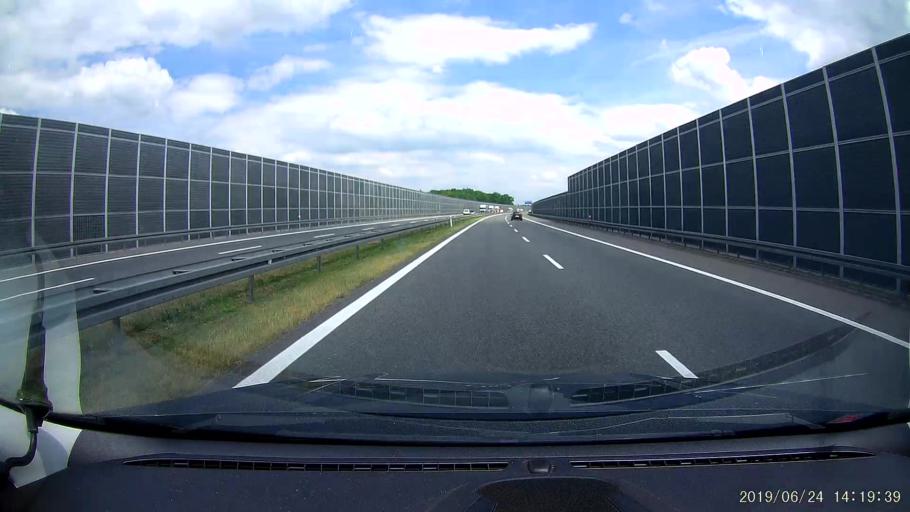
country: PL
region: Lesser Poland Voivodeship
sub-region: Powiat bochenski
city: Bochnia
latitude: 50.0040
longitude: 20.4089
